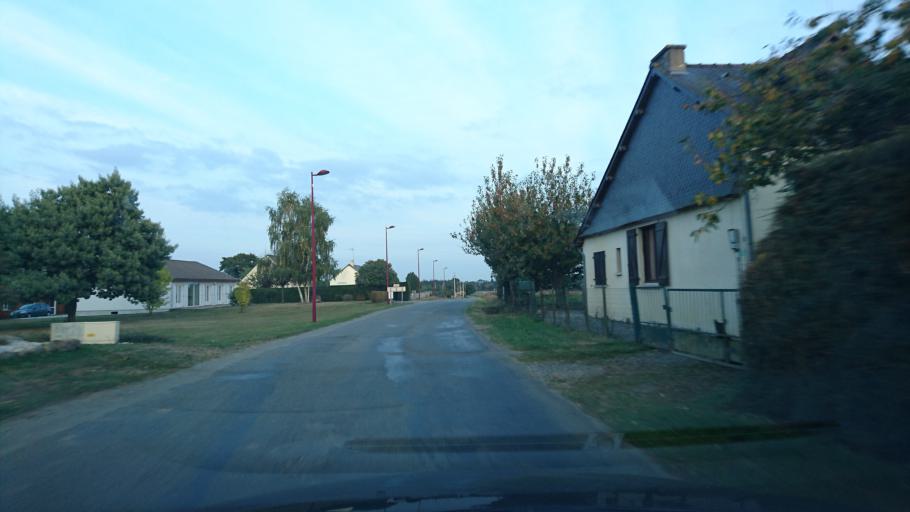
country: FR
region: Brittany
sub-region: Departement d'Ille-et-Vilaine
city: Maure-de-Bretagne
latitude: 47.8899
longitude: -2.0393
